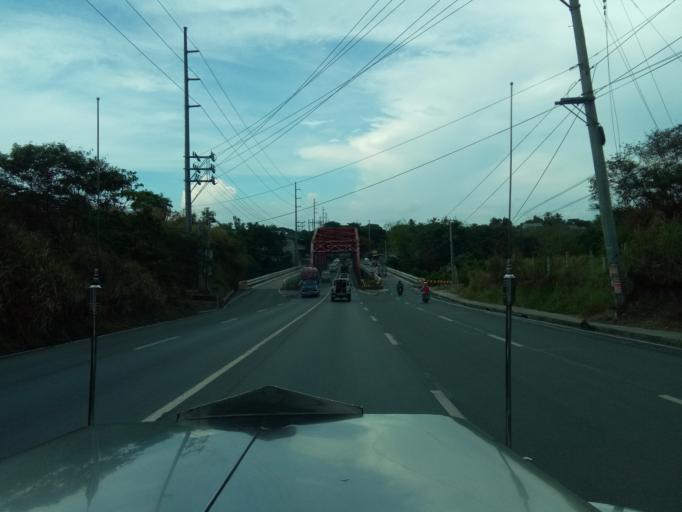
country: PH
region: Calabarzon
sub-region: Province of Cavite
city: Aliang
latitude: 14.2800
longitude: 120.8801
